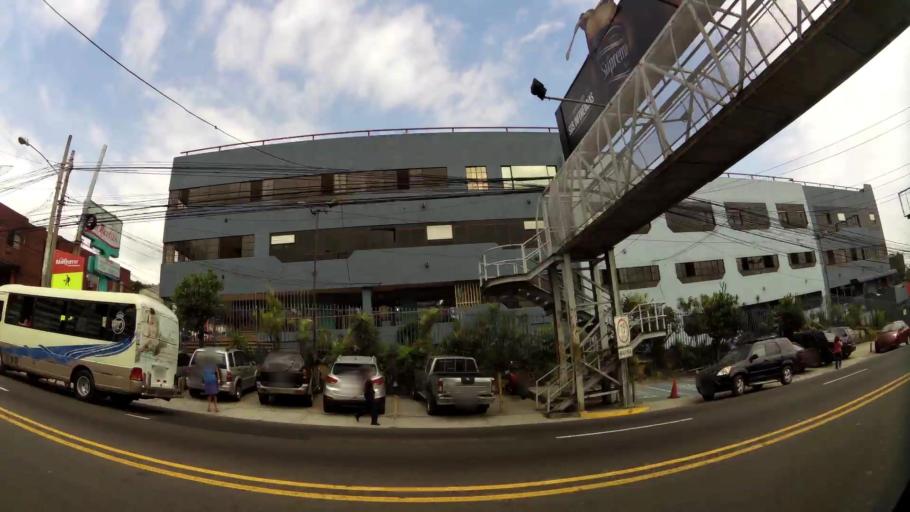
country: SV
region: La Libertad
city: Antiguo Cuscatlan
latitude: 13.7034
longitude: -89.2472
